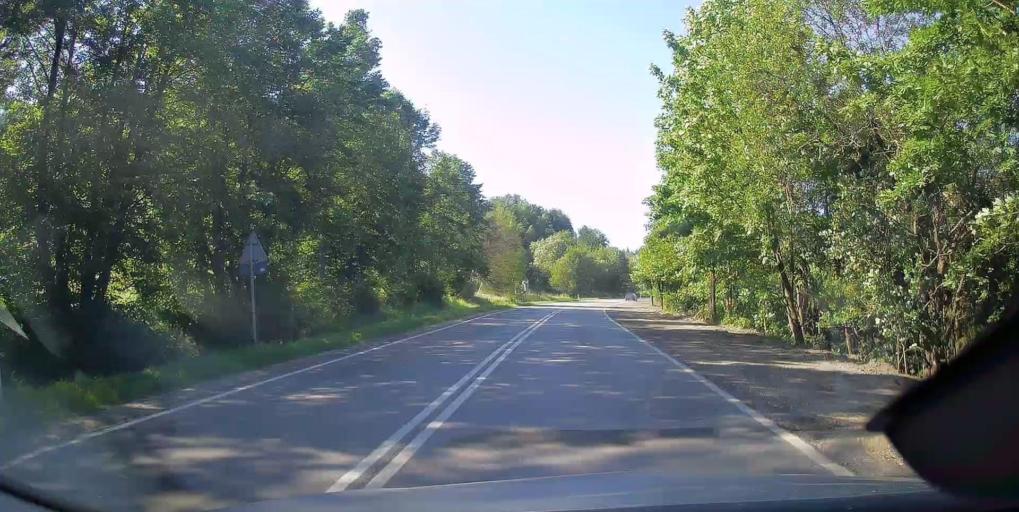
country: PL
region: Lesser Poland Voivodeship
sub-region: Powiat nowosadecki
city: Krynica-Zdroj
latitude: 49.4349
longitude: 20.9494
